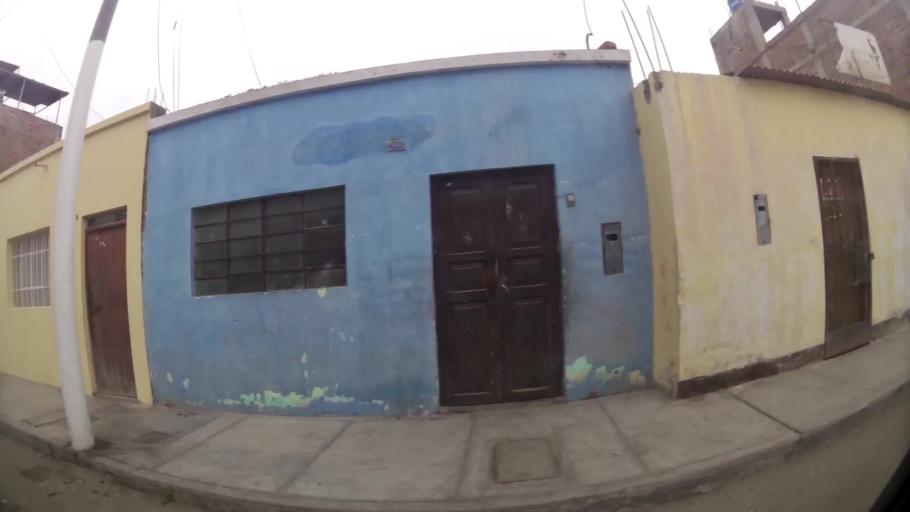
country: PE
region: La Libertad
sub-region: Provincia de Trujillo
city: Trujillo
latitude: -8.1053
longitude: -79.0396
